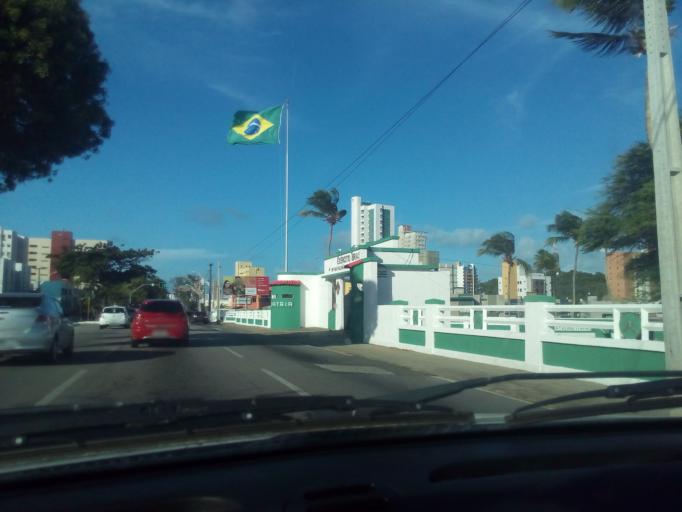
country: BR
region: Rio Grande do Norte
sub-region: Natal
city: Natal
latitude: -5.8020
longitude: -35.2012
